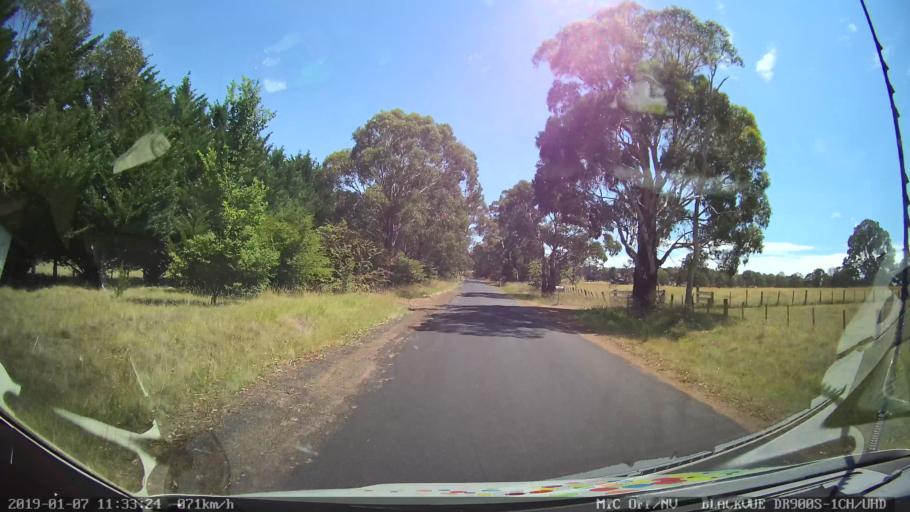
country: AU
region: New South Wales
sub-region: Armidale Dumaresq
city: Armidale
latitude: -30.4004
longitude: 151.5610
